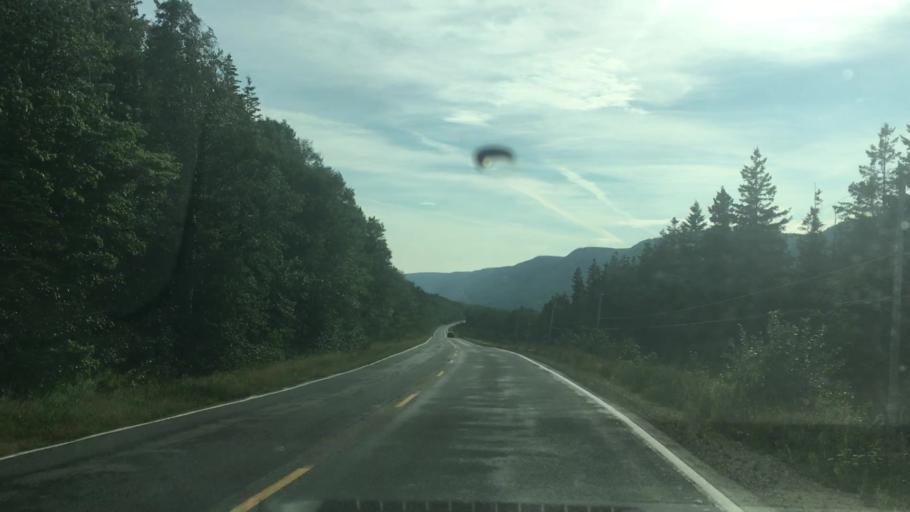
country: CA
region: Nova Scotia
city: Sydney Mines
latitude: 46.8655
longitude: -60.5605
